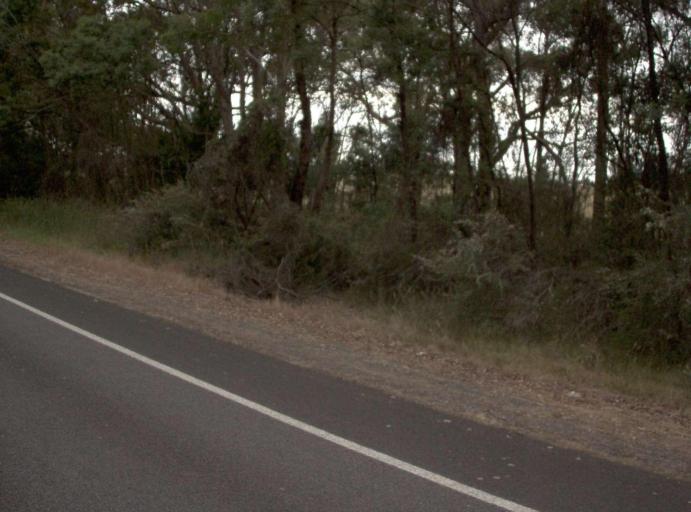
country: AU
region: Victoria
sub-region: Wellington
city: Sale
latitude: -38.5112
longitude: 146.8875
